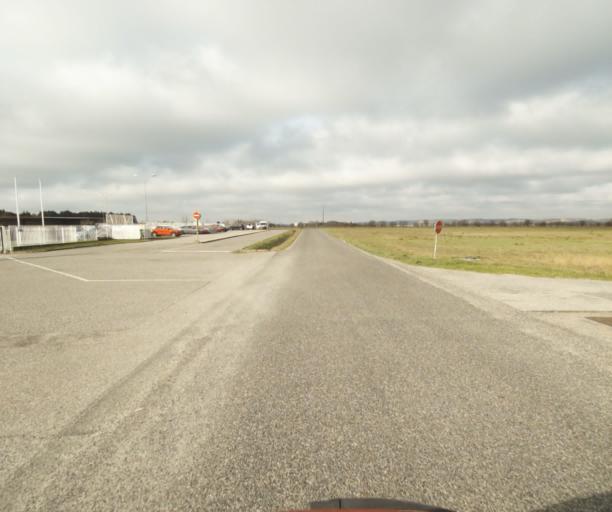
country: FR
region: Midi-Pyrenees
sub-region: Departement de l'Ariege
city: Mazeres
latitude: 43.2125
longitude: 1.6907
